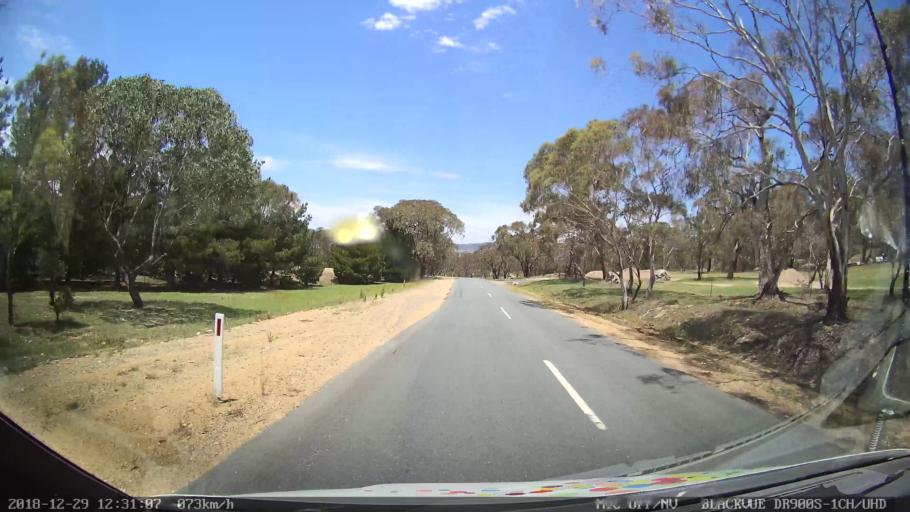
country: AU
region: Australian Capital Territory
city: Macarthur
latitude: -35.5127
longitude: 149.2325
